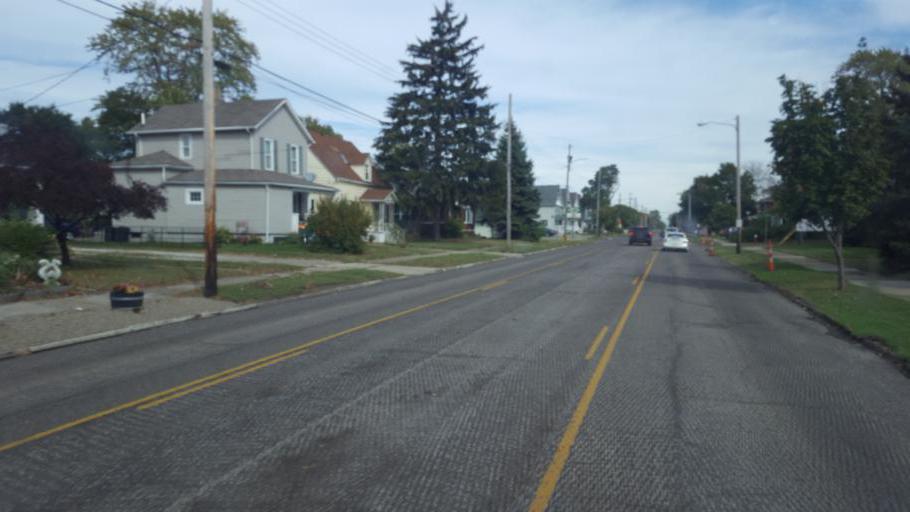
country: US
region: Ohio
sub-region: Lorain County
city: Lorain
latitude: 41.4723
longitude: -82.1689
